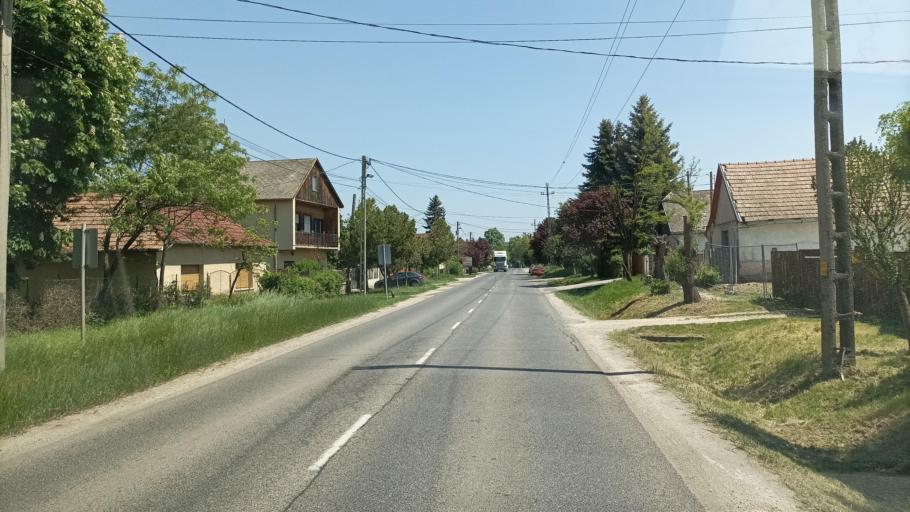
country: HU
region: Pest
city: Gyomro
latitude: 47.4141
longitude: 19.3914
